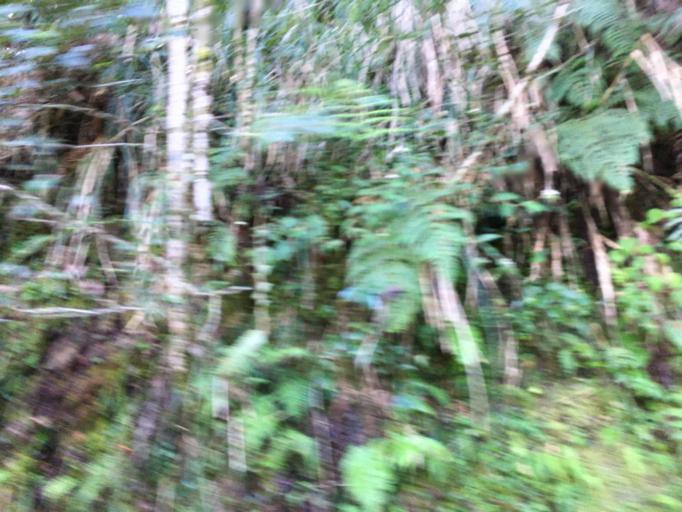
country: TW
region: Taiwan
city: Daxi
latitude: 24.5504
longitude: 121.3983
